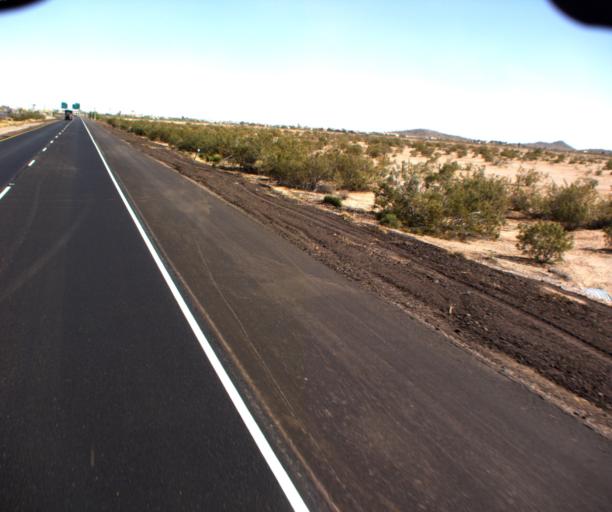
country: US
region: Arizona
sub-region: Pinal County
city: Arizona City
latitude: 32.8228
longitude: -111.6933
